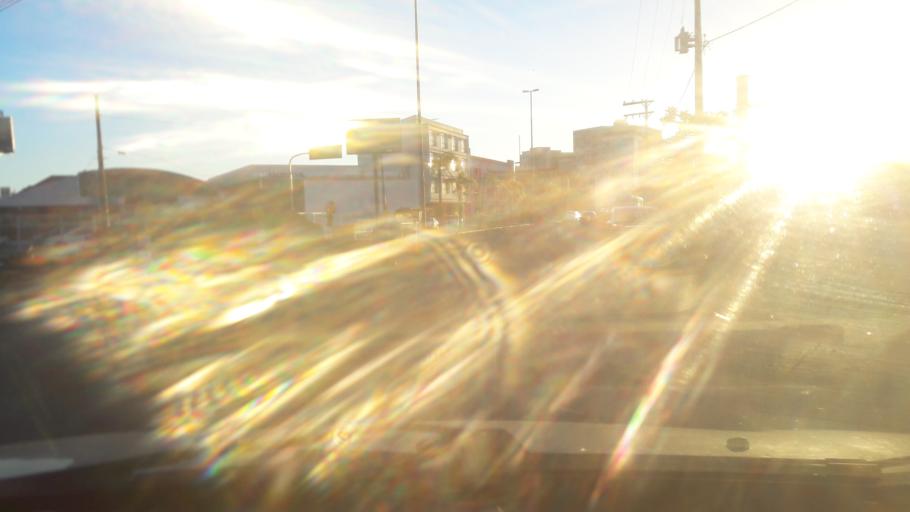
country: BR
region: Rio Grande do Sul
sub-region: Porto Alegre
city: Porto Alegre
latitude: -29.9962
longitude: -51.1899
